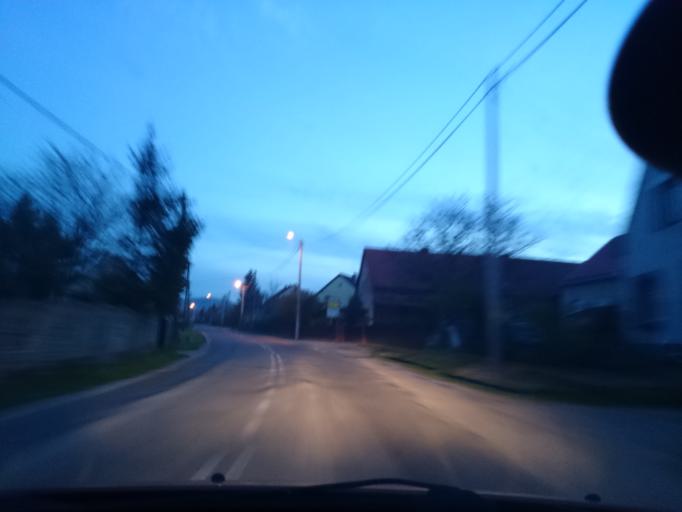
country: PL
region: Lower Silesian Voivodeship
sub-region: Powiat zabkowicki
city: Budzow
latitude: 50.5891
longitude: 16.7020
